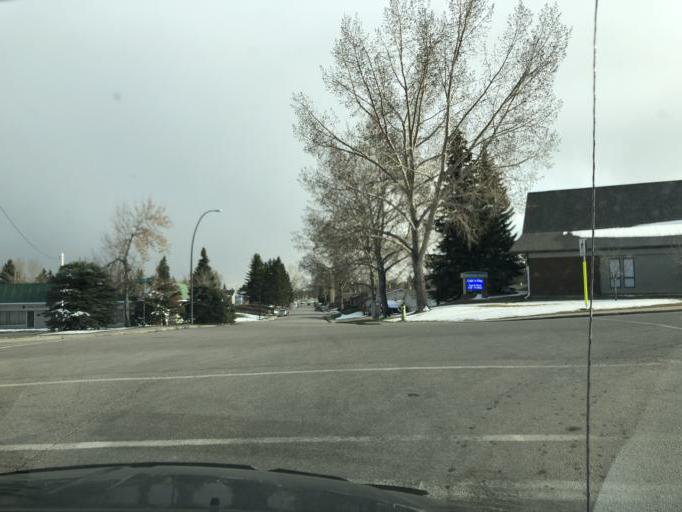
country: CA
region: Alberta
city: Calgary
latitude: 50.9427
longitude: -114.0338
